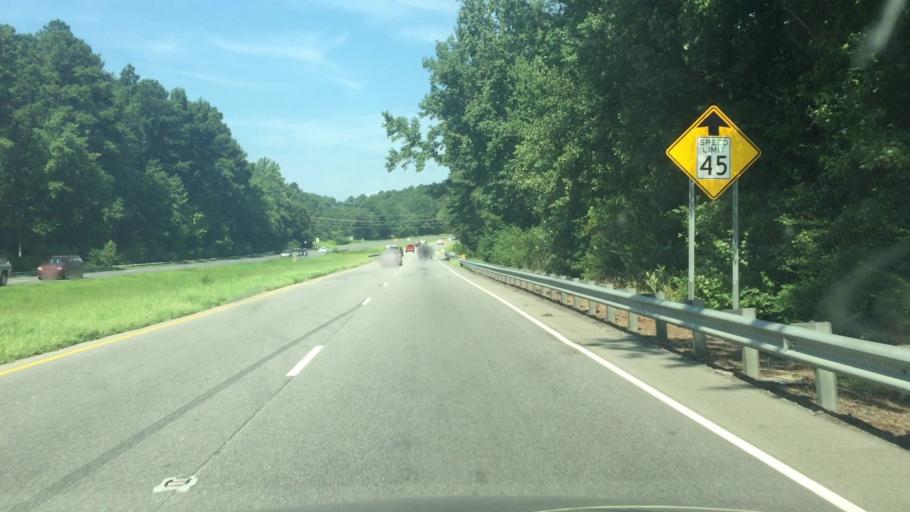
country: US
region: North Carolina
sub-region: Scotland County
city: Laurel Hill
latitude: 34.7996
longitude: -79.5296
